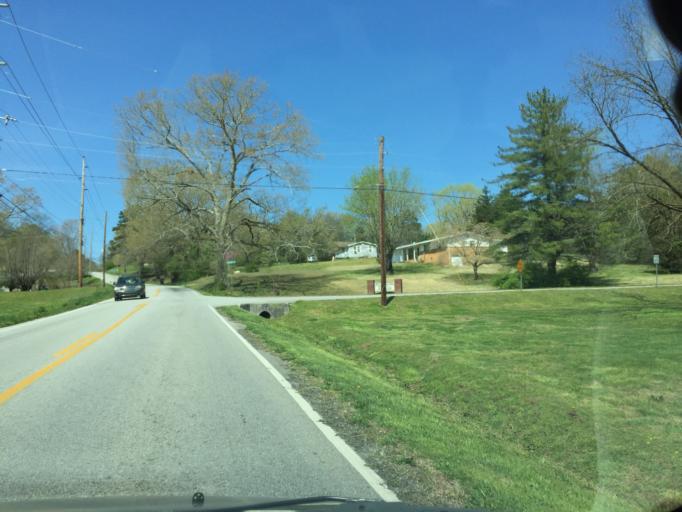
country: US
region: Tennessee
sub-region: Hamilton County
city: Middle Valley
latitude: 35.1939
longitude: -85.1950
